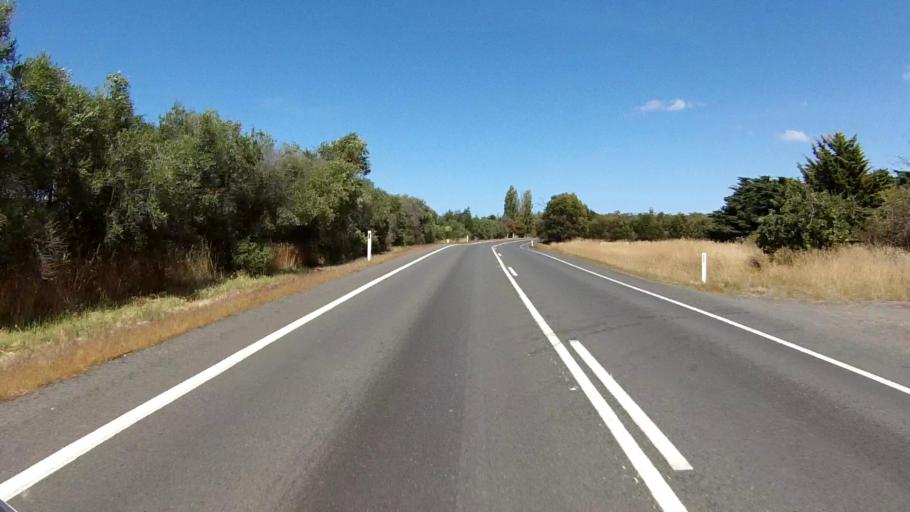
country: AU
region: Tasmania
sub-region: Break O'Day
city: St Helens
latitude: -42.0725
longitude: 148.0668
